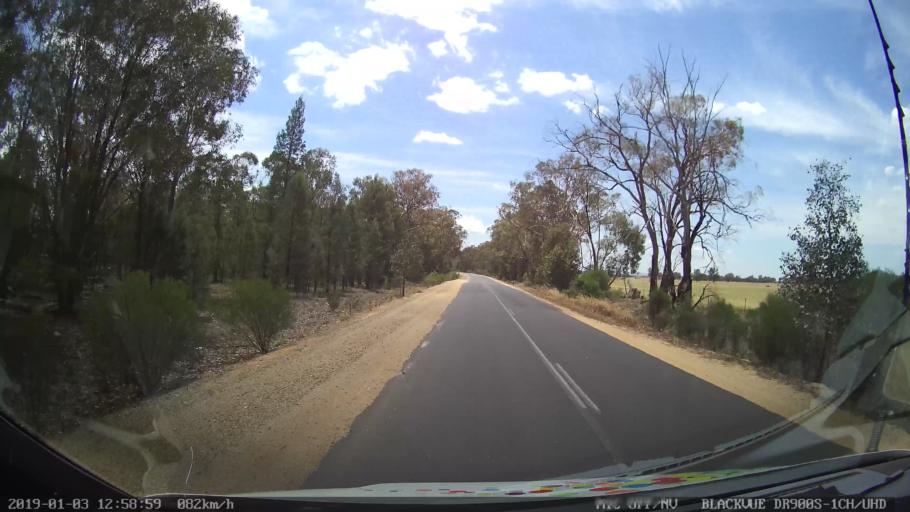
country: AU
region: New South Wales
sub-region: Cabonne
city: Canowindra
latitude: -33.6395
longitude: 148.3830
